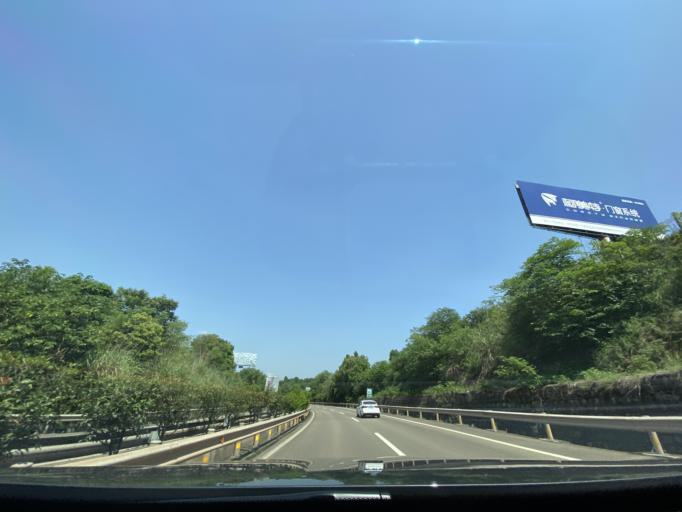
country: CN
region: Sichuan
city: Longquan
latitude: 30.4858
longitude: 104.3996
